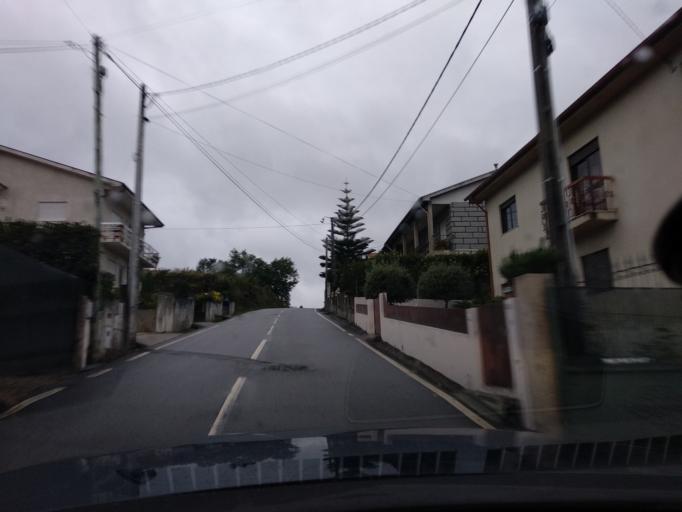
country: PT
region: Porto
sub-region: Penafiel
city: Penafiel
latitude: 41.1964
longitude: -8.2800
